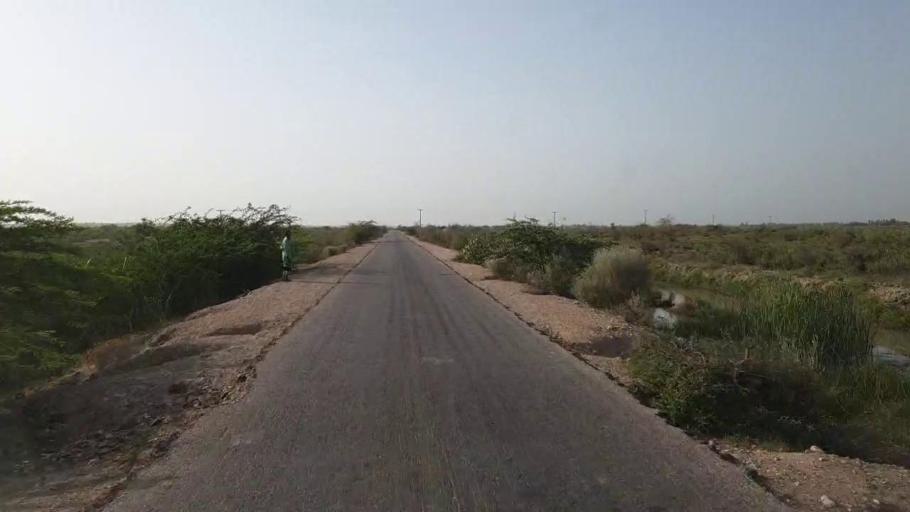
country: PK
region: Sindh
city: Jam Sahib
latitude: 26.4501
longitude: 68.8628
